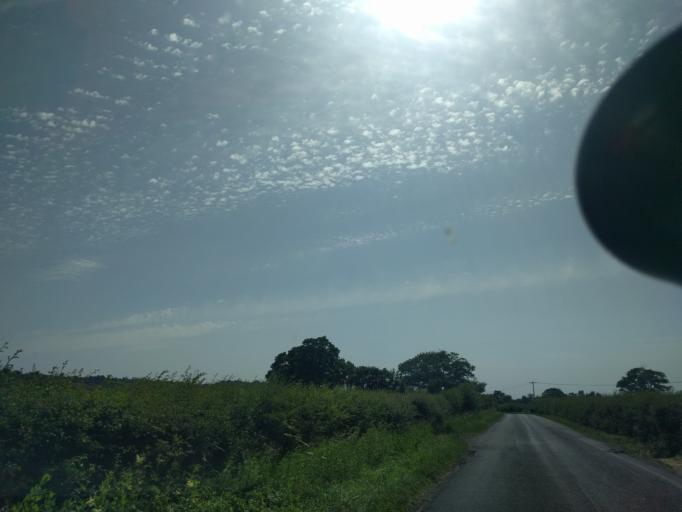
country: GB
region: England
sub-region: Wiltshire
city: Lyneham
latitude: 51.5369
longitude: -1.9765
